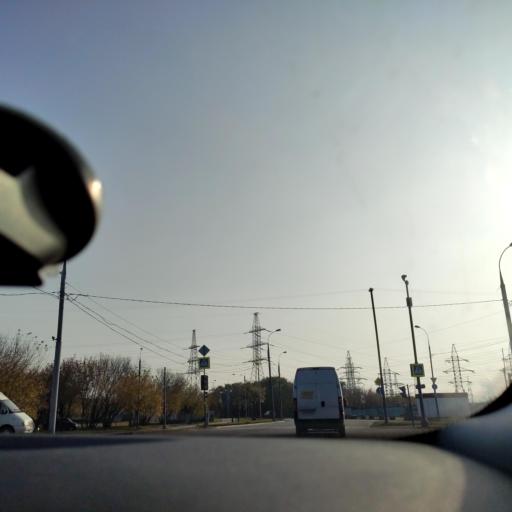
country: RU
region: Moscow
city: Kuz'minki
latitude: 55.6748
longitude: 37.7980
